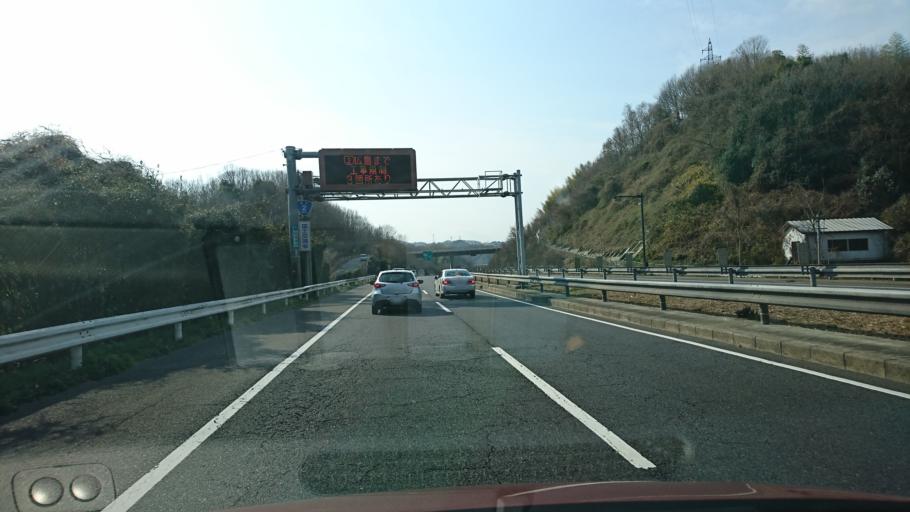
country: JP
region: Hiroshima
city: Onomichi
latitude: 34.4386
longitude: 133.2256
